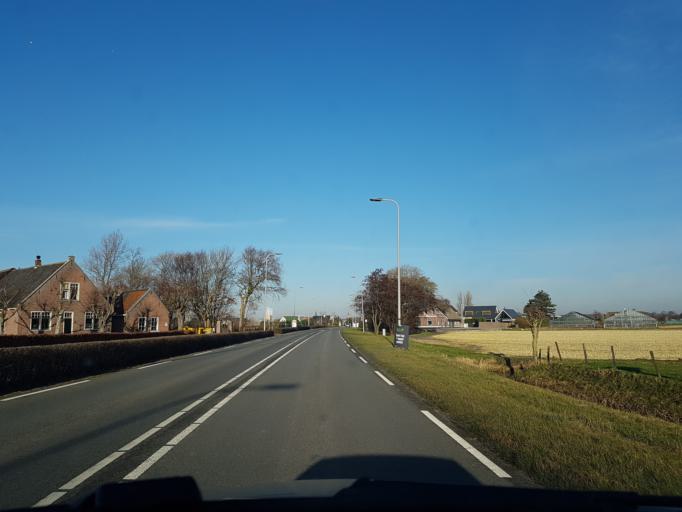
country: NL
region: South Holland
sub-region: Gemeente Noordwijk
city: Noordwijk-Binnen
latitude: 52.2191
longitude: 4.4390
